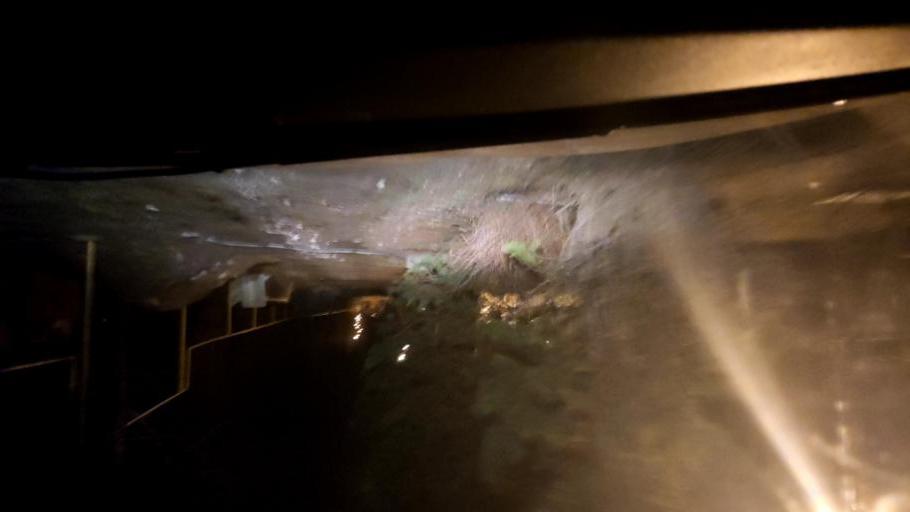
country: RU
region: Perm
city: Perm
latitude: 58.0531
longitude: 56.3627
